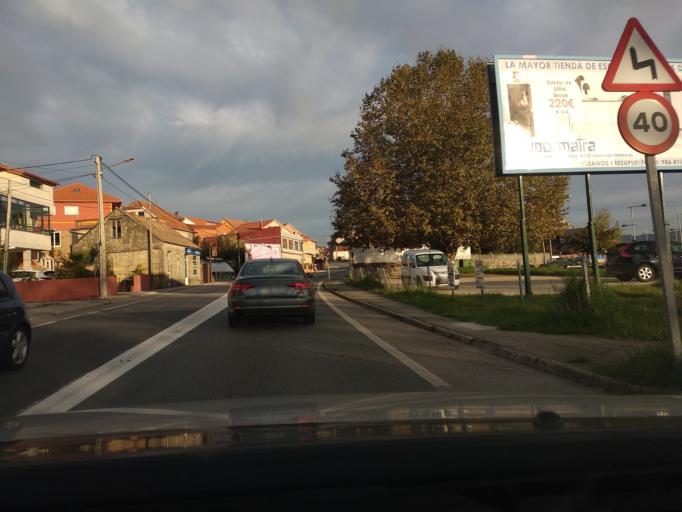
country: ES
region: Galicia
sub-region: Provincia de Pontevedra
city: Moana
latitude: 42.2870
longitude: -8.7250
